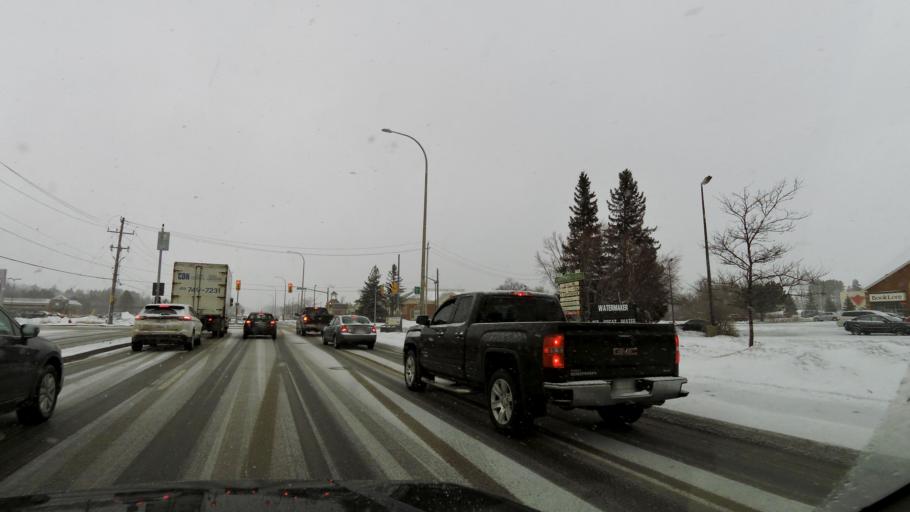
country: CA
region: Ontario
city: Orangeville
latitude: 43.9303
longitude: -80.1002
